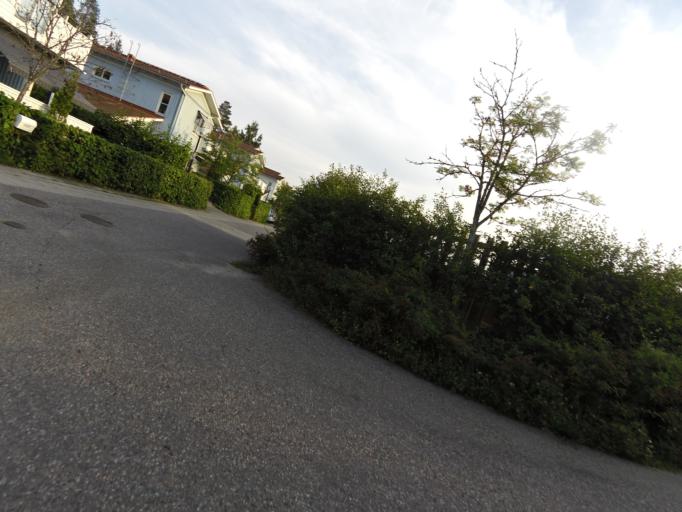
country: SE
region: Gaevleborg
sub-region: Gavle Kommun
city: Gavle
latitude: 60.7031
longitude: 17.1034
